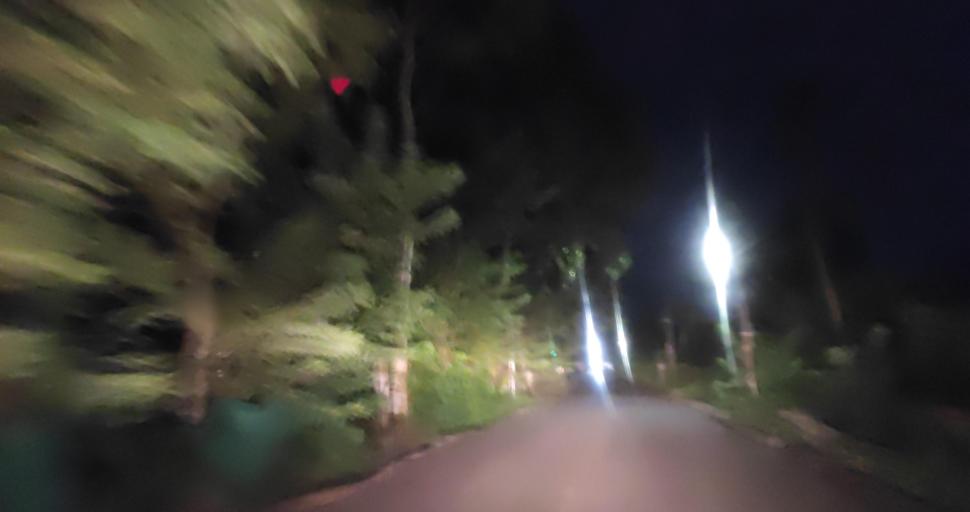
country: IN
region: Kerala
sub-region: Alappuzha
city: Vayalar
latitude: 9.6729
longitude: 76.3043
